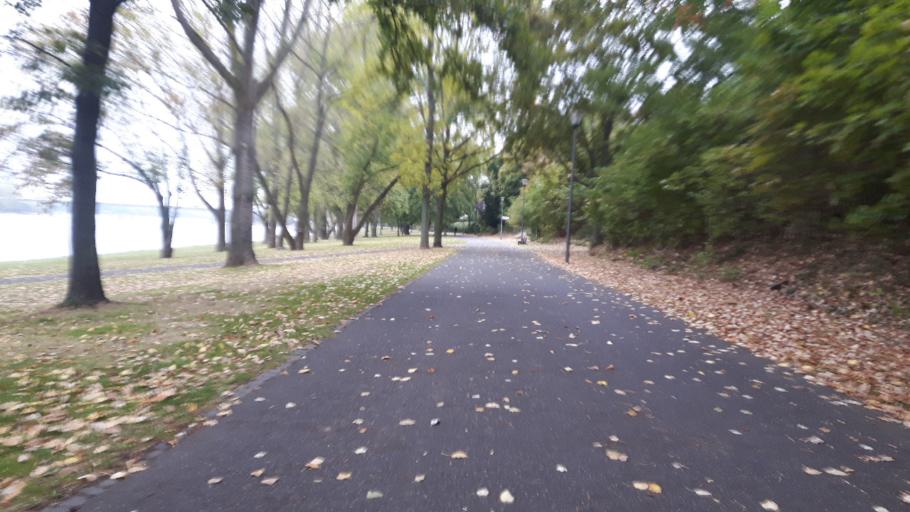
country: DE
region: North Rhine-Westphalia
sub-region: Regierungsbezirk Koln
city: Konigswinter
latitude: 50.7136
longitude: 7.1602
